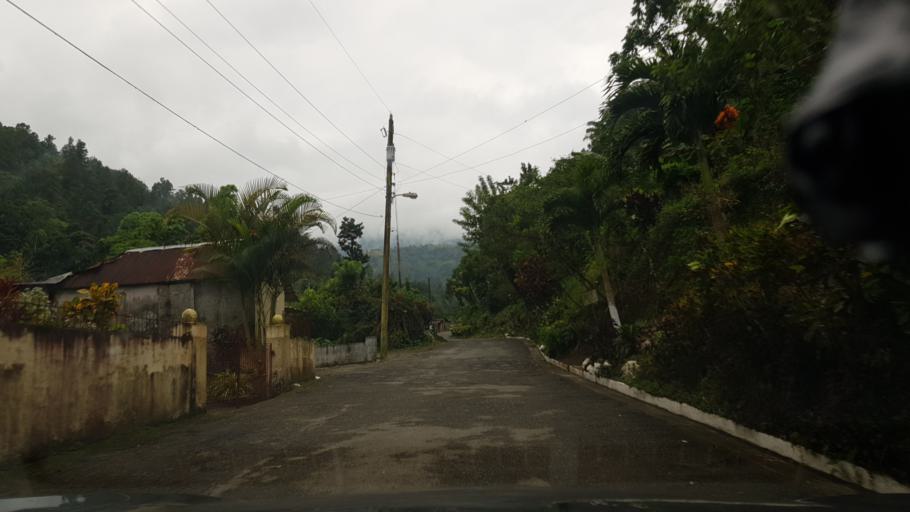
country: JM
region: Saint Andrew
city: Stony Hill
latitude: 18.1231
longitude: -76.7153
